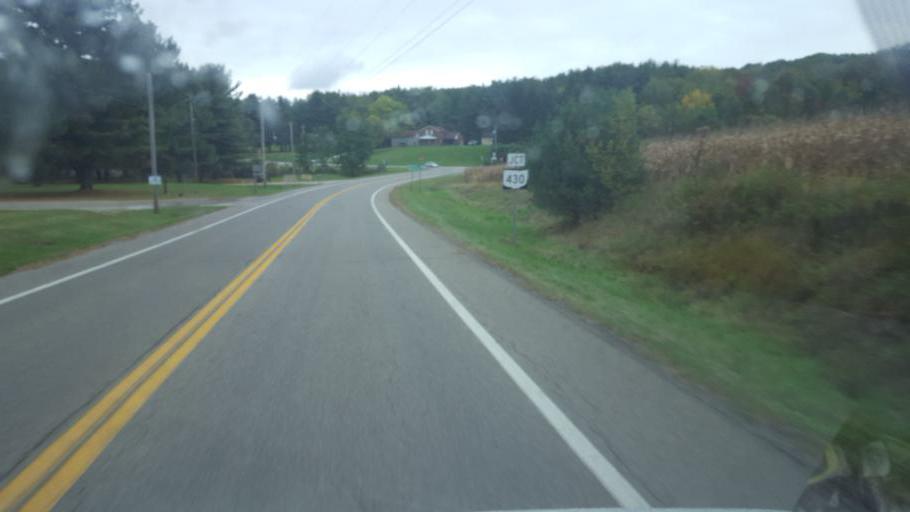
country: US
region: Ohio
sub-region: Richland County
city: Lincoln Heights
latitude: 40.7573
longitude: -82.4786
